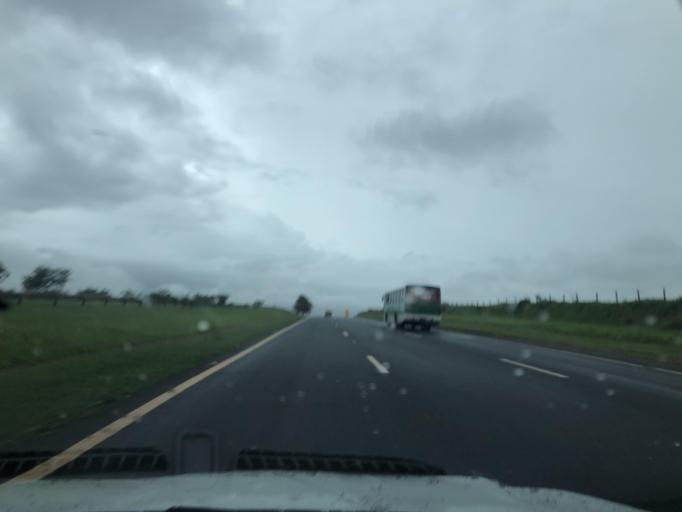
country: BR
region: Sao Paulo
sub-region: Jardinopolis
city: Jardinopolis
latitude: -21.0131
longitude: -47.8443
